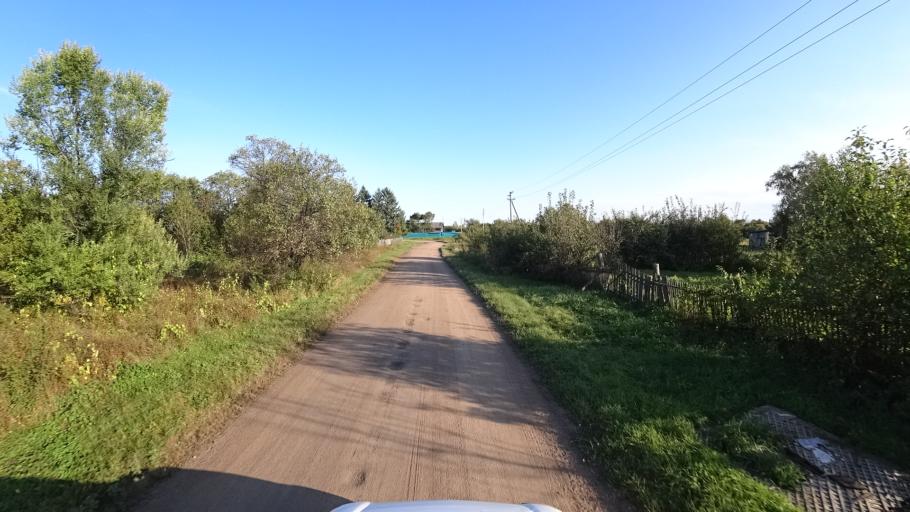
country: RU
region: Amur
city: Arkhara
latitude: 49.3617
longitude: 130.1244
